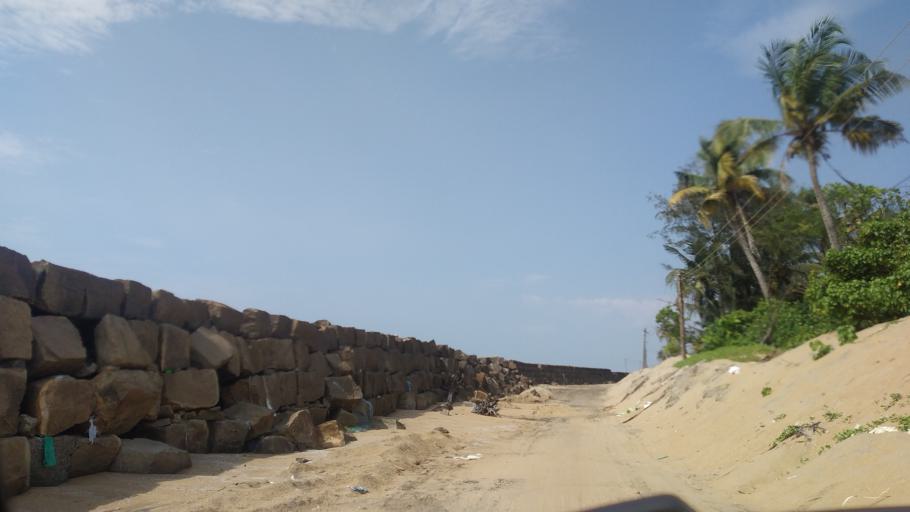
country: IN
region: Kerala
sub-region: Ernakulam
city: Elur
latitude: 10.0858
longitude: 76.1931
